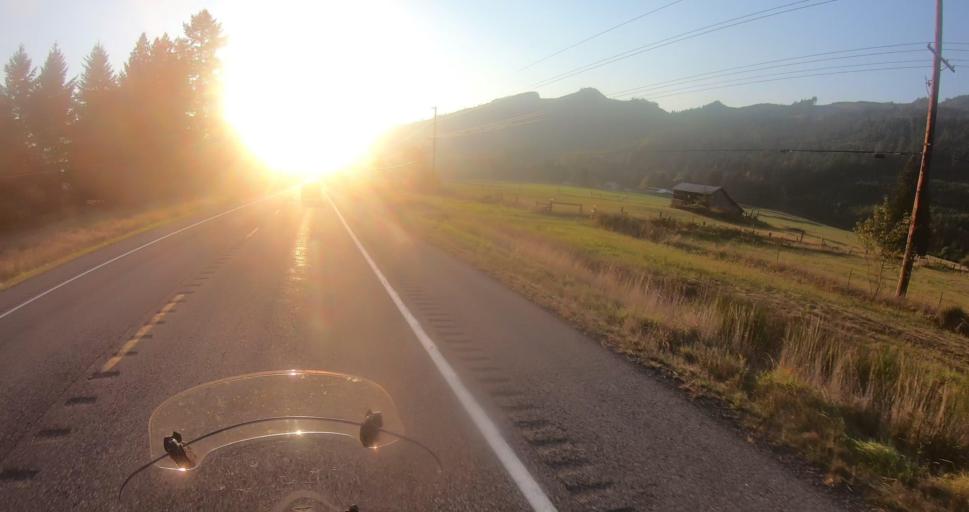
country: US
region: Washington
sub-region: Lewis County
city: Morton
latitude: 46.5387
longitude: -122.1043
